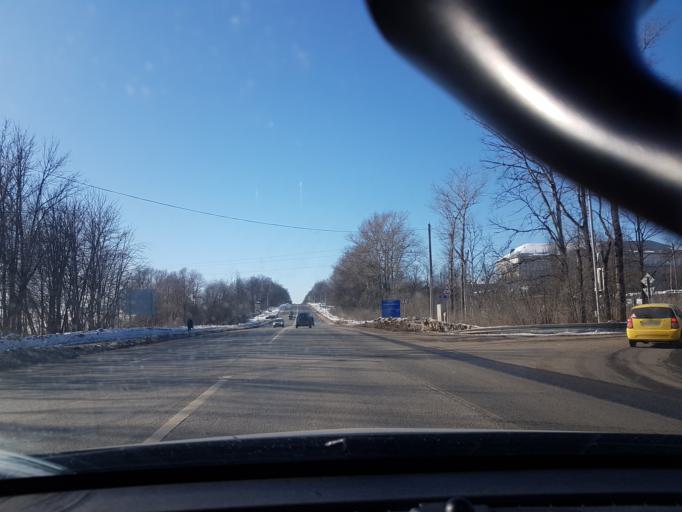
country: RU
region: Moskovskaya
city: Istra
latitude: 55.9081
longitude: 36.7969
